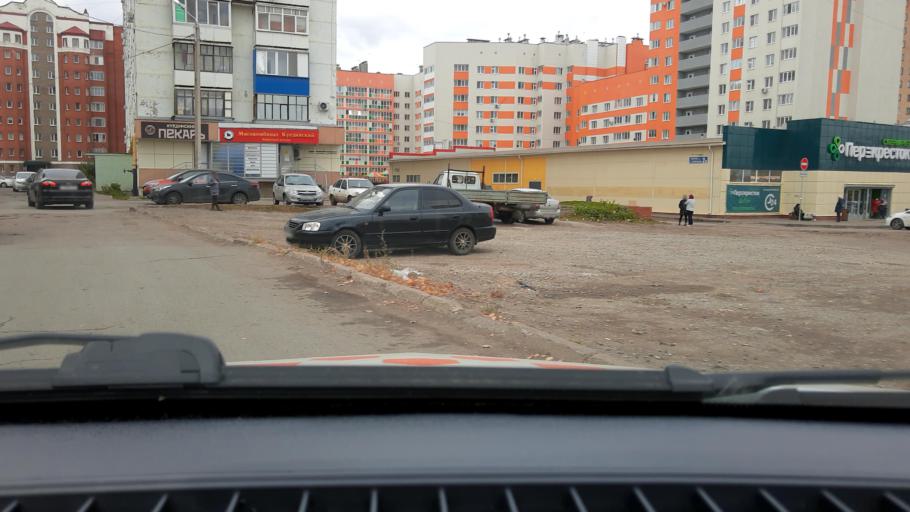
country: RU
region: Bashkortostan
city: Mikhaylovka
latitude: 54.7104
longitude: 55.8345
